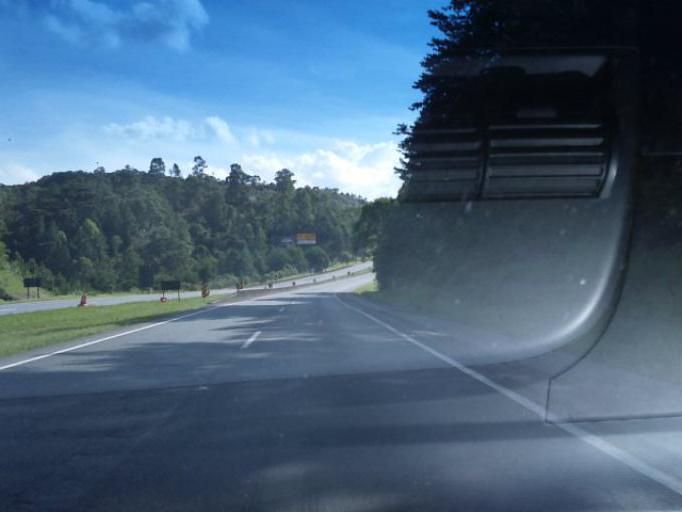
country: BR
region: Parana
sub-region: Campina Grande Do Sul
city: Campina Grande do Sul
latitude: -25.1939
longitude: -48.8889
